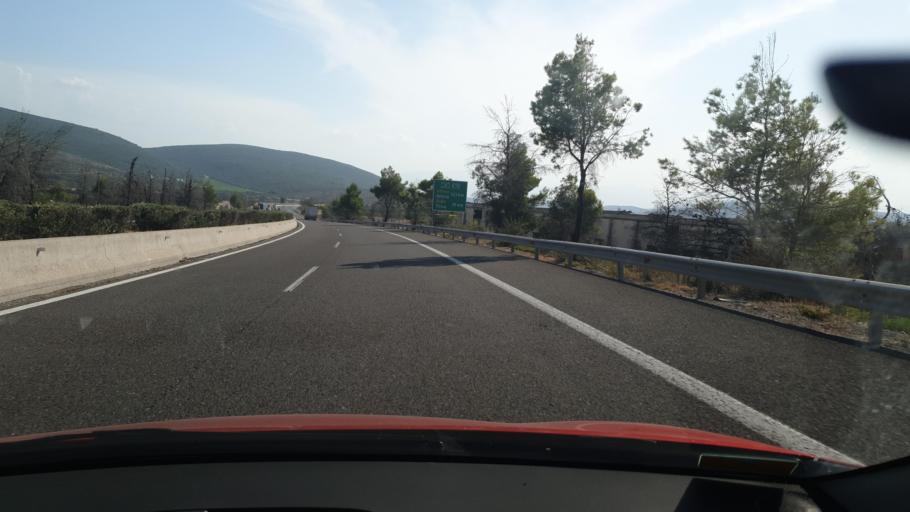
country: GR
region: Central Greece
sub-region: Nomos Fthiotidos
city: Martinon
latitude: 38.5687
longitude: 23.1918
